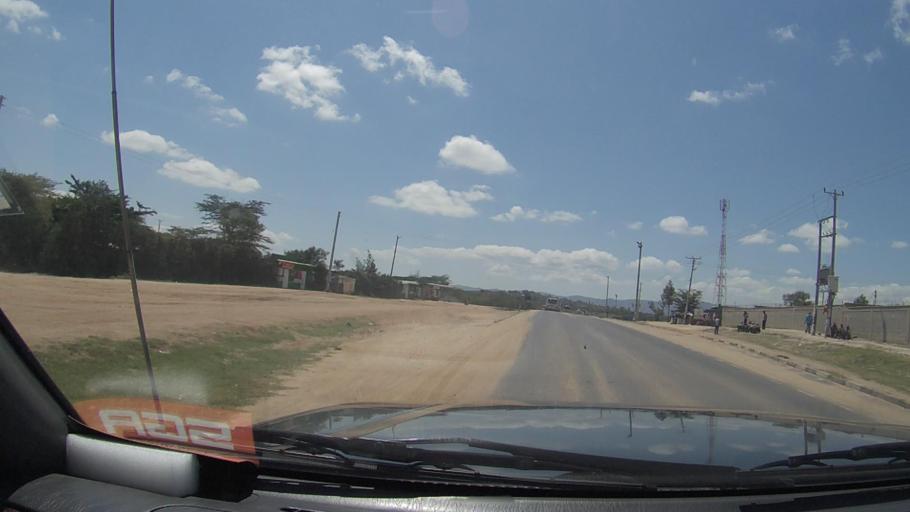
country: KE
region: Machakos
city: Machakos
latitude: -1.5329
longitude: 37.1970
